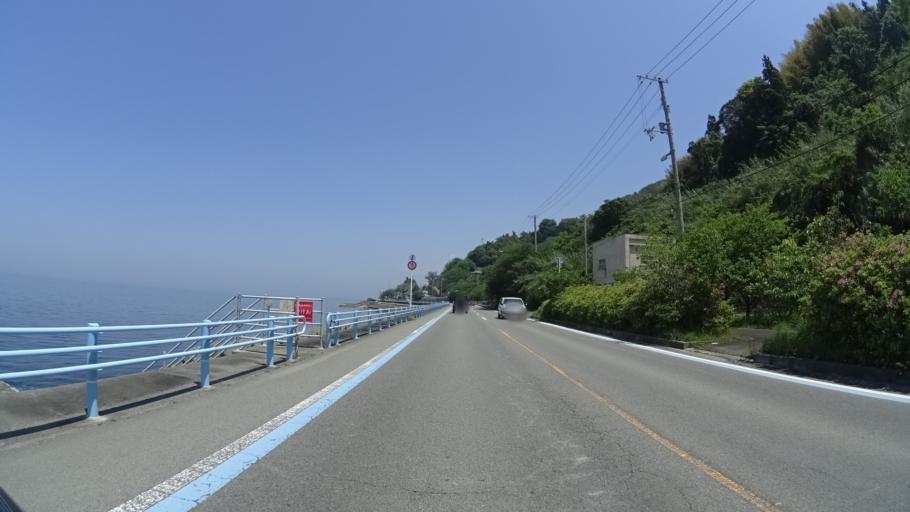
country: JP
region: Ehime
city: Iyo
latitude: 33.6681
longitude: 132.6085
